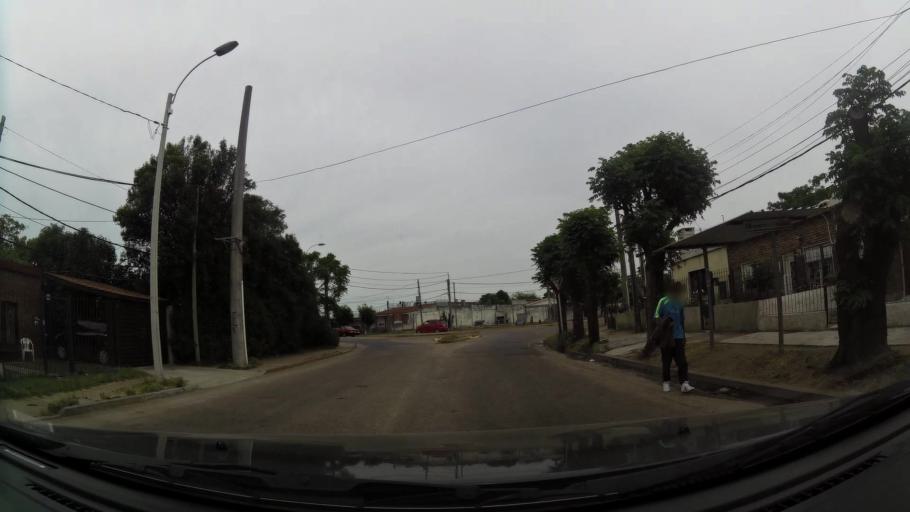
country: UY
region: Canelones
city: Las Piedras
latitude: -34.7342
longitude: -56.2165
